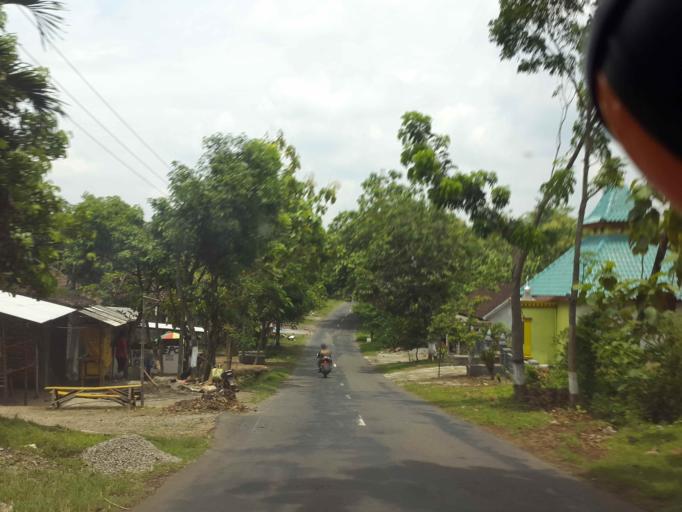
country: ID
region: East Java
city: Ponorogo
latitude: -7.7222
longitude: 111.3559
